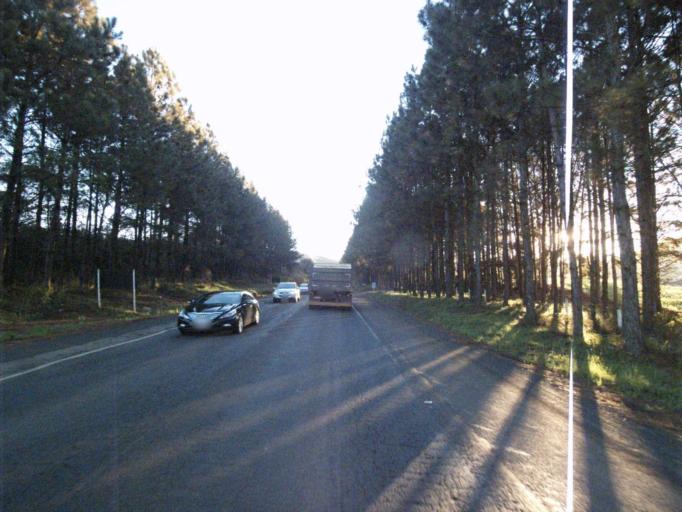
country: BR
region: Santa Catarina
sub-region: Sao Lourenco Do Oeste
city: Sao Lourenco dOeste
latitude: -26.8294
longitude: -53.1326
